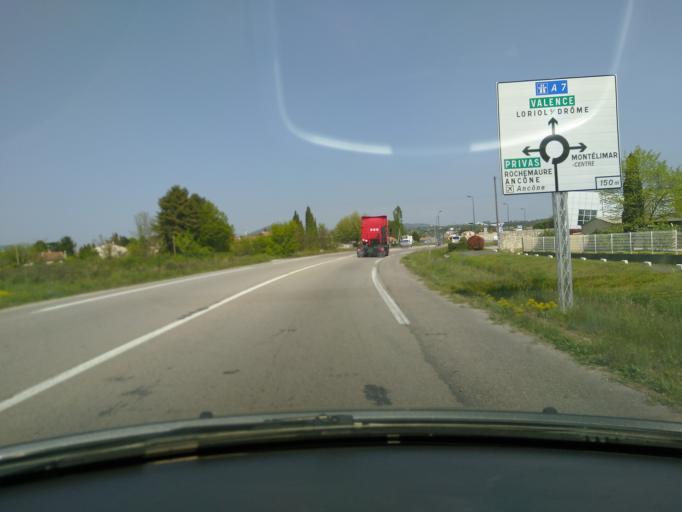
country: FR
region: Rhone-Alpes
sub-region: Departement de la Drome
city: Ancone
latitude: 44.5651
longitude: 4.7331
